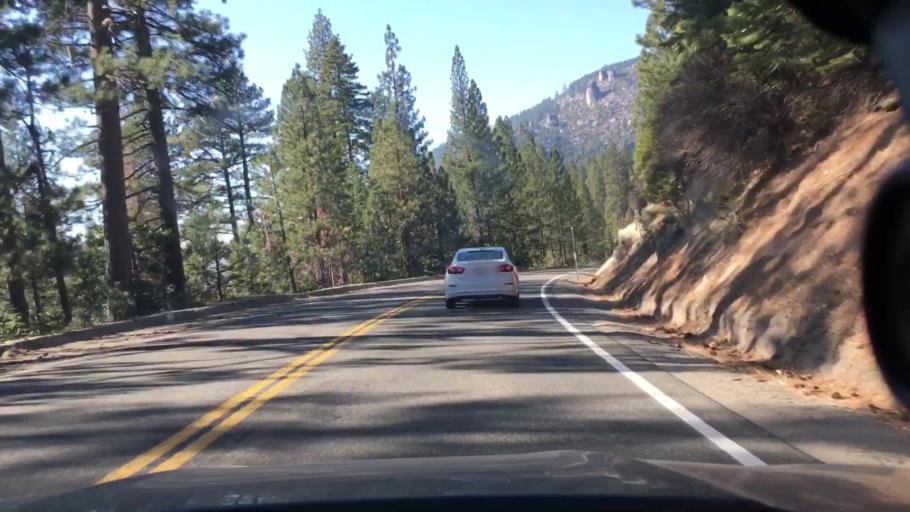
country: US
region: California
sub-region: El Dorado County
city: South Lake Tahoe
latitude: 38.7822
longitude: -120.2200
